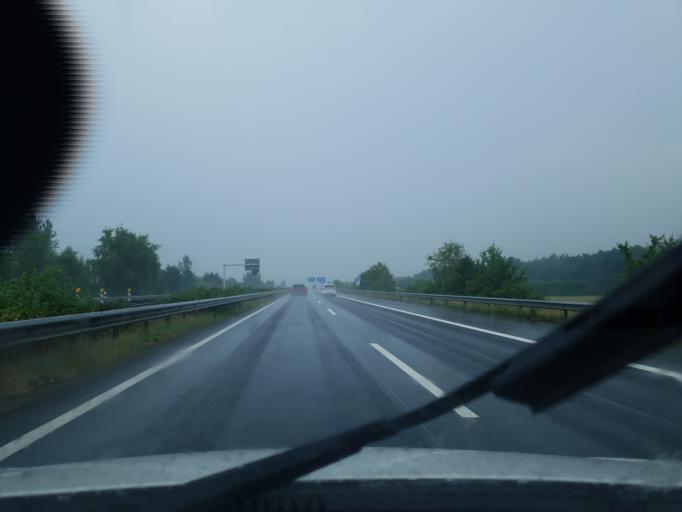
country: DE
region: Lower Saxony
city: Schuttorf
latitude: 52.3325
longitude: 7.2575
